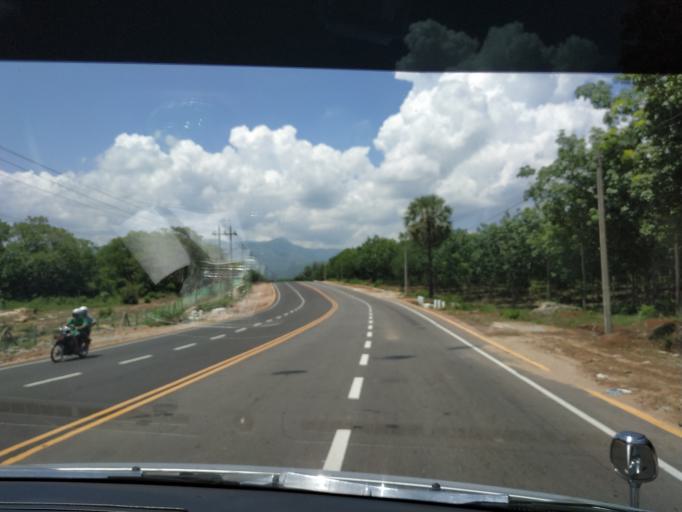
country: MM
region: Mon
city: Kyaikto
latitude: 17.3726
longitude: 97.0509
